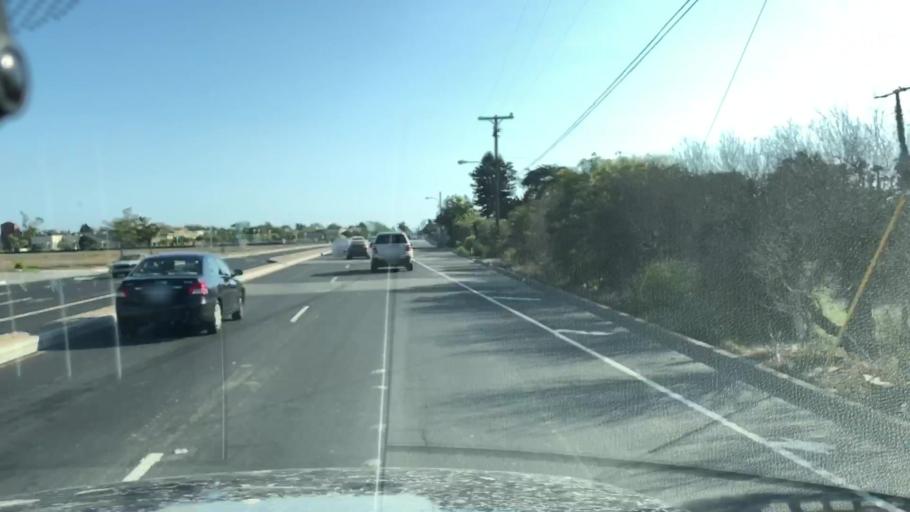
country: US
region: California
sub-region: Ventura County
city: Oxnard
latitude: 34.2026
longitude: -119.1948
